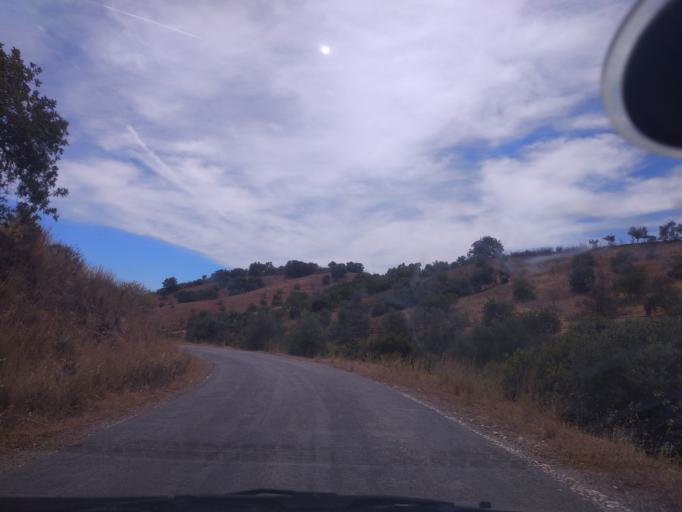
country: PT
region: Faro
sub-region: Olhao
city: Moncarapacho
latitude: 37.1693
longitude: -7.8039
